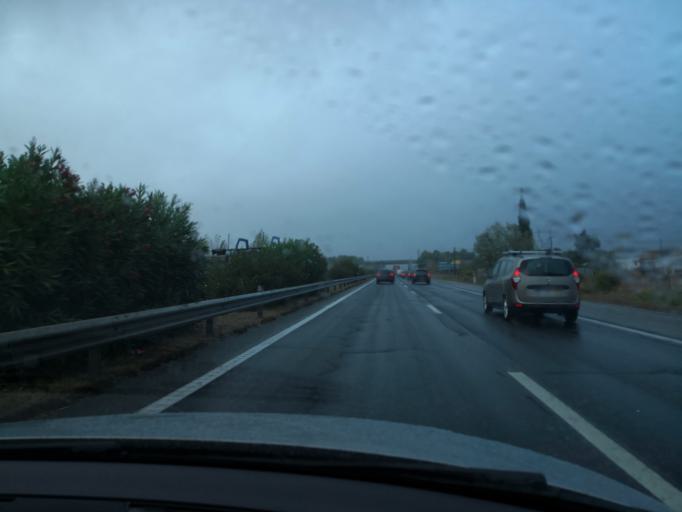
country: PT
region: Setubal
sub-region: Moita
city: Moita
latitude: 38.6572
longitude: -8.9633
